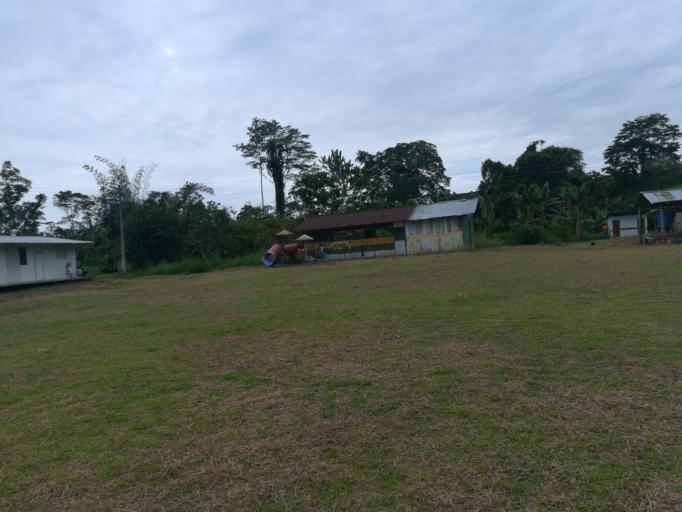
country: EC
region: Orellana
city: Boca Suno
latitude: -0.7496
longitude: -77.1539
